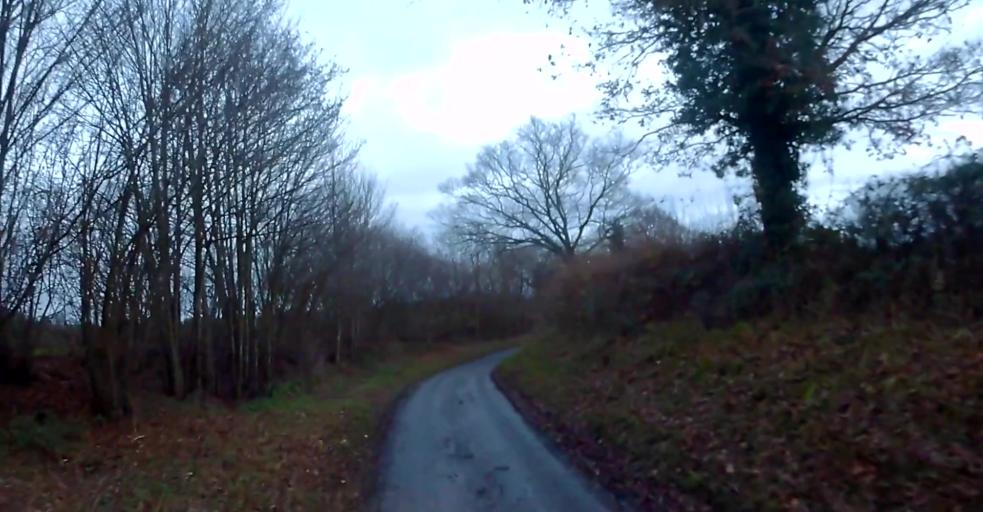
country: GB
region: England
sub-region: Hampshire
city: Overton
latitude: 51.2558
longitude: -1.2169
